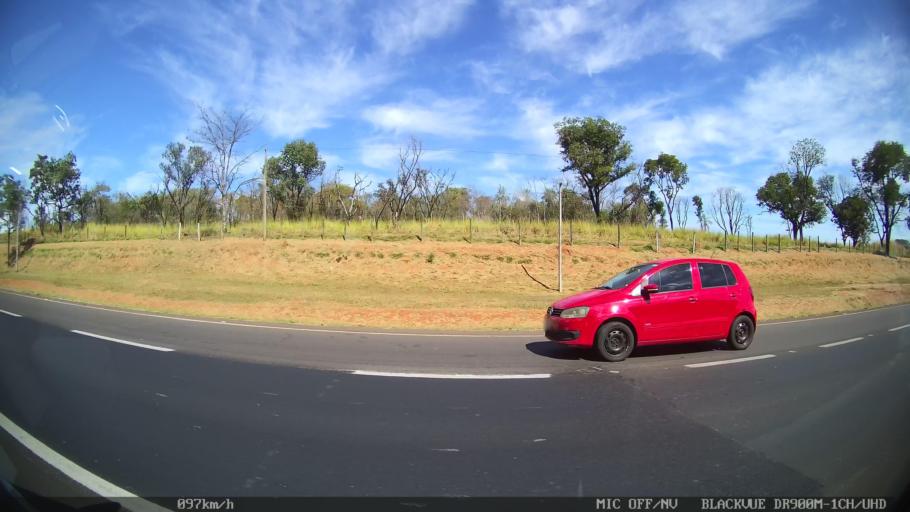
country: BR
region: Sao Paulo
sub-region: Sao Jose Do Rio Preto
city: Sao Jose do Rio Preto
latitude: -20.8198
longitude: -49.4323
